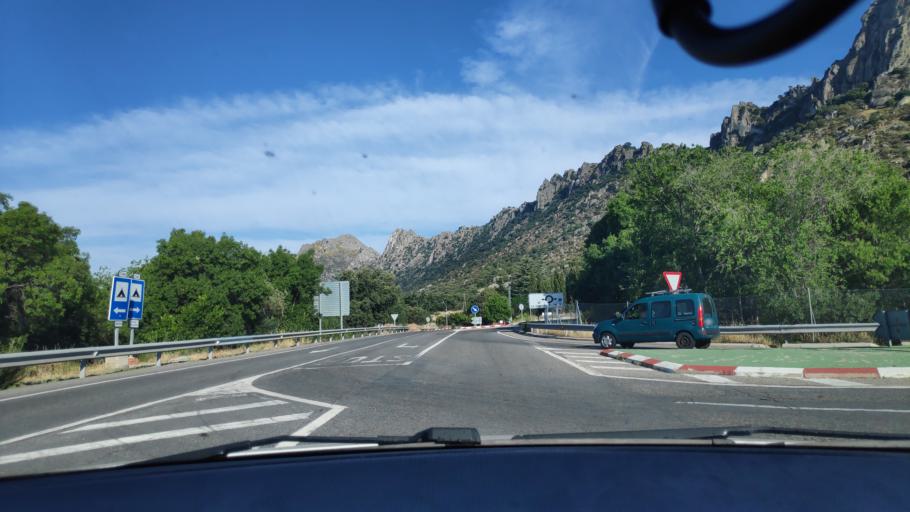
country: ES
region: Madrid
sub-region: Provincia de Madrid
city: La Cabrera
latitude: 40.8742
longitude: -3.6029
